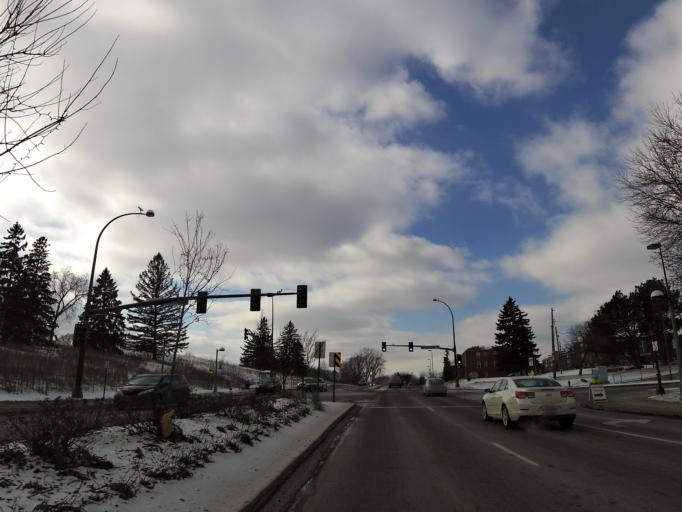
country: US
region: Minnesota
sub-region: Hennepin County
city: Saint Louis Park
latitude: 44.9271
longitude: -93.3644
